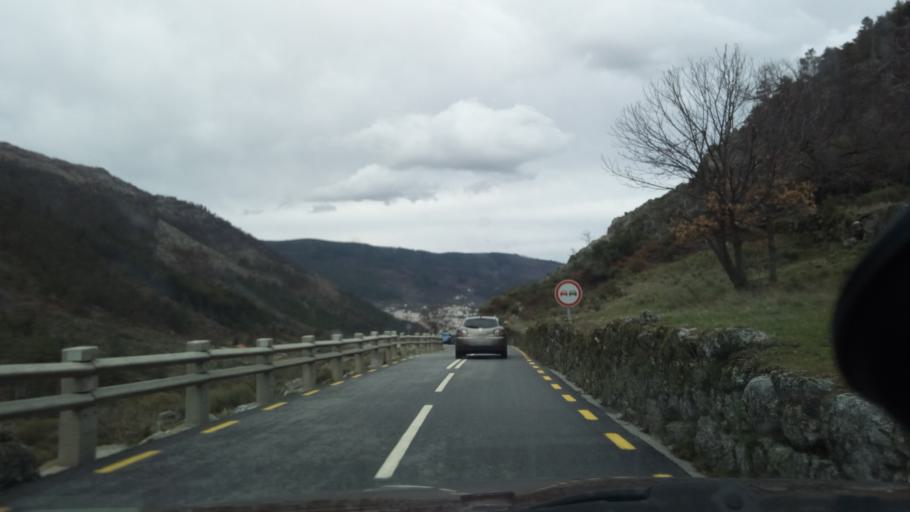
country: PT
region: Guarda
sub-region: Manteigas
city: Manteigas
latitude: 40.3705
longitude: -7.5501
